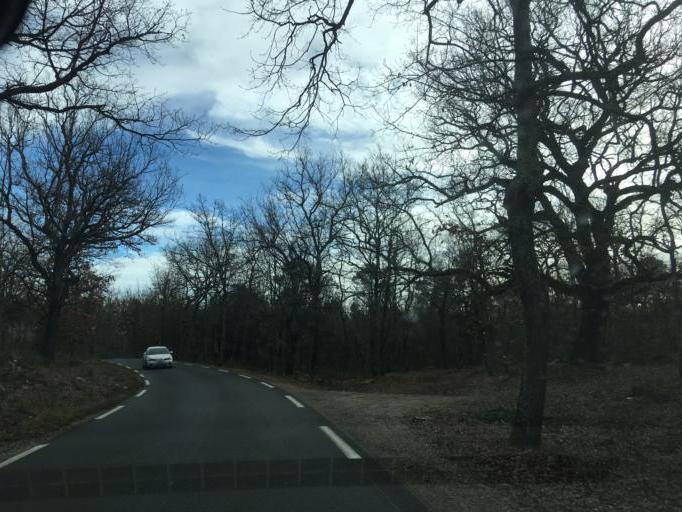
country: FR
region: Provence-Alpes-Cote d'Azur
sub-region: Departement du Var
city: Bras
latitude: 43.4490
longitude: 5.9846
